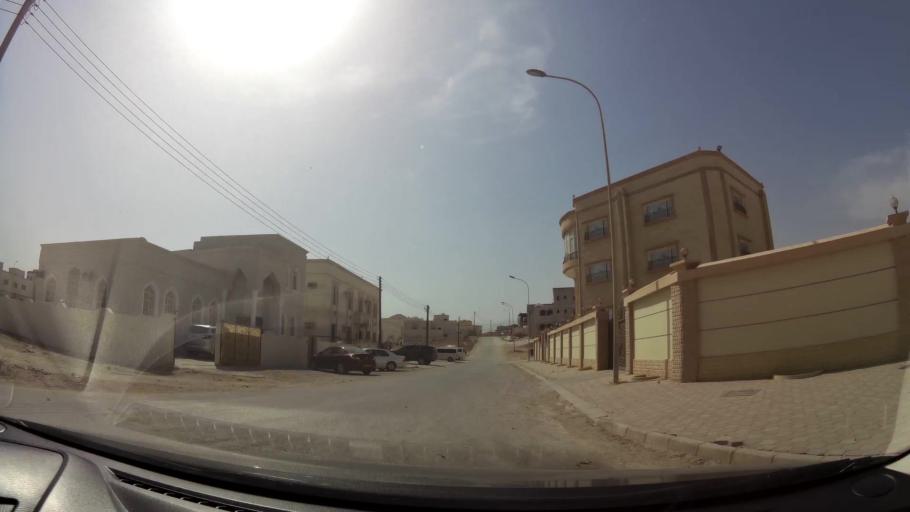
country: OM
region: Zufar
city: Salalah
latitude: 17.0008
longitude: 54.0190
